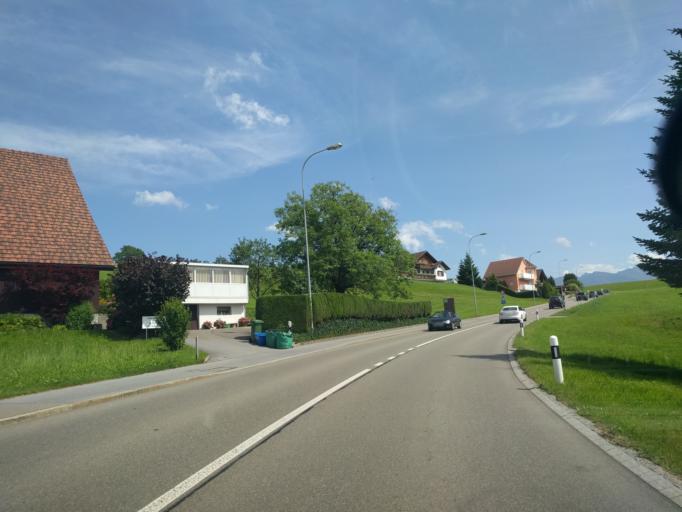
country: CH
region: Saint Gallen
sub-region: Wahlkreis See-Gaster
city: Gommiswald
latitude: 47.2508
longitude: 9.0092
